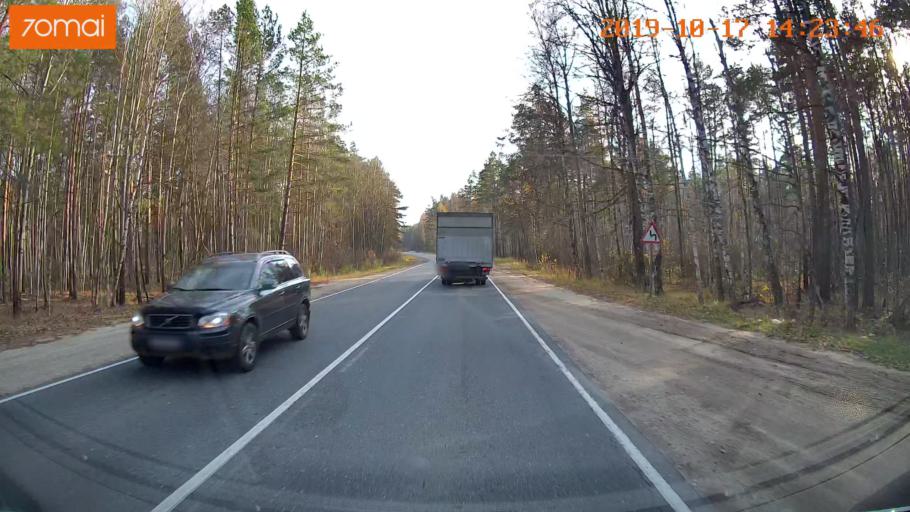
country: RU
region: Moskovskaya
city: Radovitskiy
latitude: 55.0154
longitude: 39.9625
